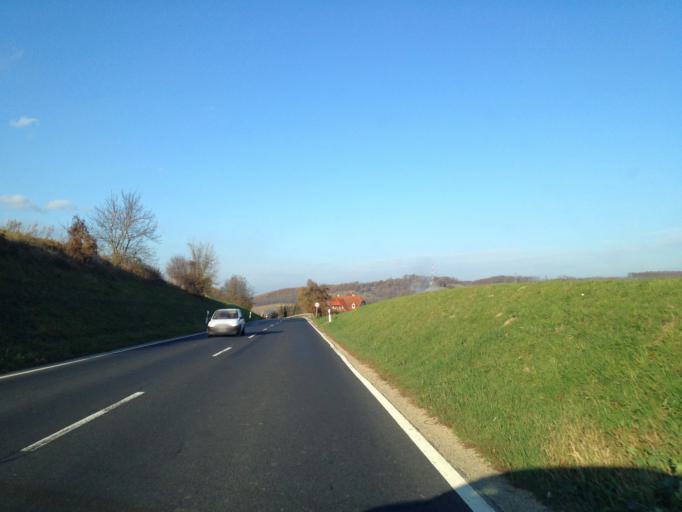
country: HU
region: Gyor-Moson-Sopron
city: Bakonyszentlaszlo
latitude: 47.3622
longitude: 17.8740
